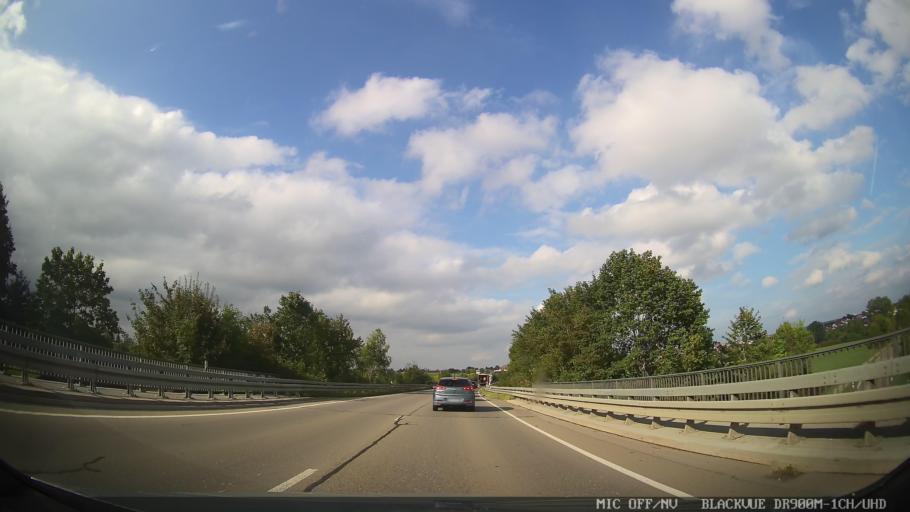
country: DE
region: Baden-Wuerttemberg
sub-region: Freiburg Region
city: Zimmern ob Rottweil
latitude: 48.1581
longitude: 8.6021
